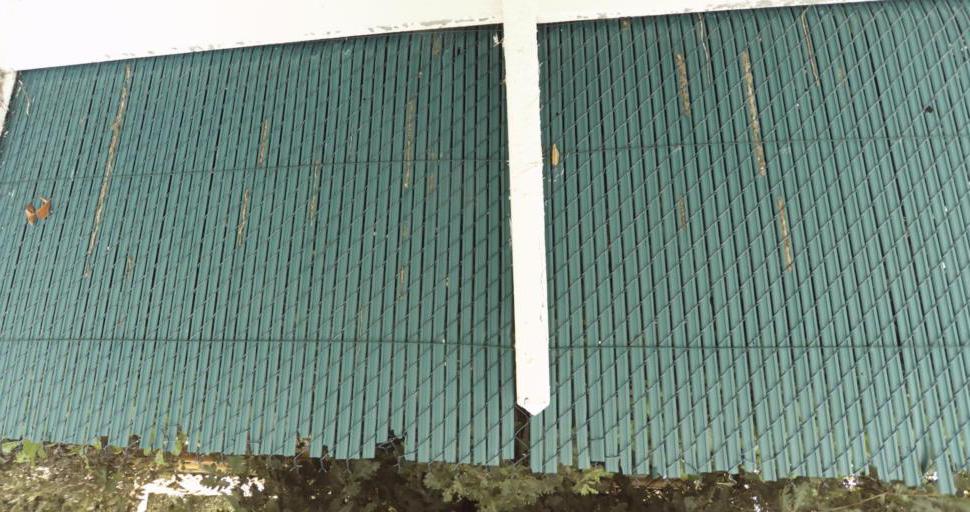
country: FR
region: Midi-Pyrenees
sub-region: Departement de la Haute-Garonne
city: Fonsorbes
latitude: 43.5564
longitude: 1.2271
